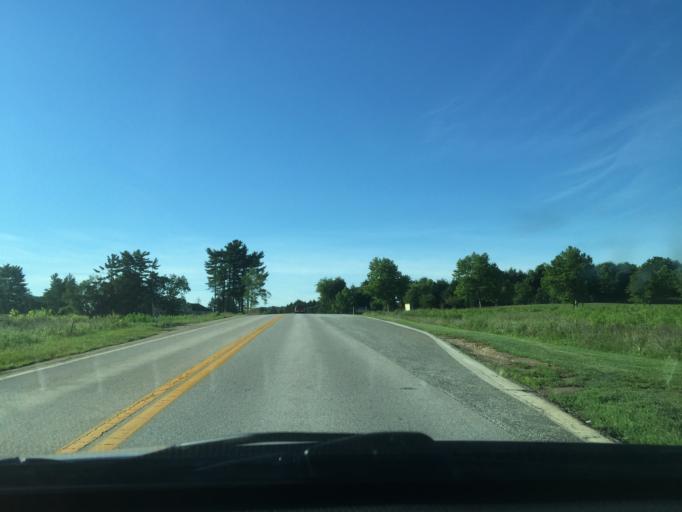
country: US
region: Maryland
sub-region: Baltimore County
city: Hunt Valley
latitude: 39.5459
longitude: -76.6614
